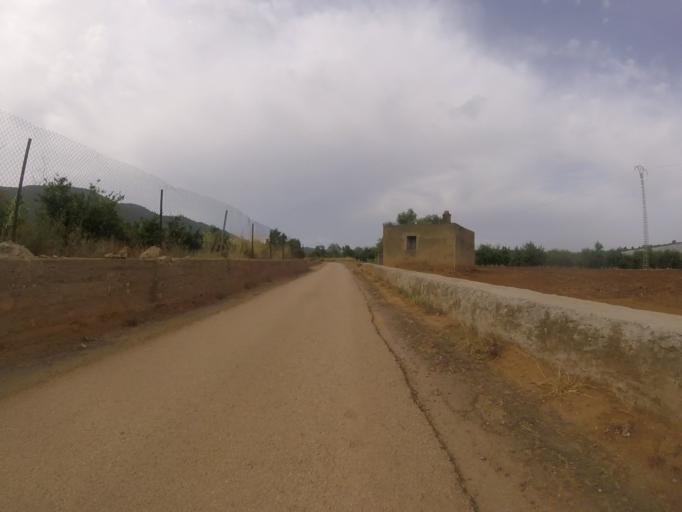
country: ES
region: Valencia
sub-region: Provincia de Castello
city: Alcala de Xivert
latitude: 40.2767
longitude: 0.2582
